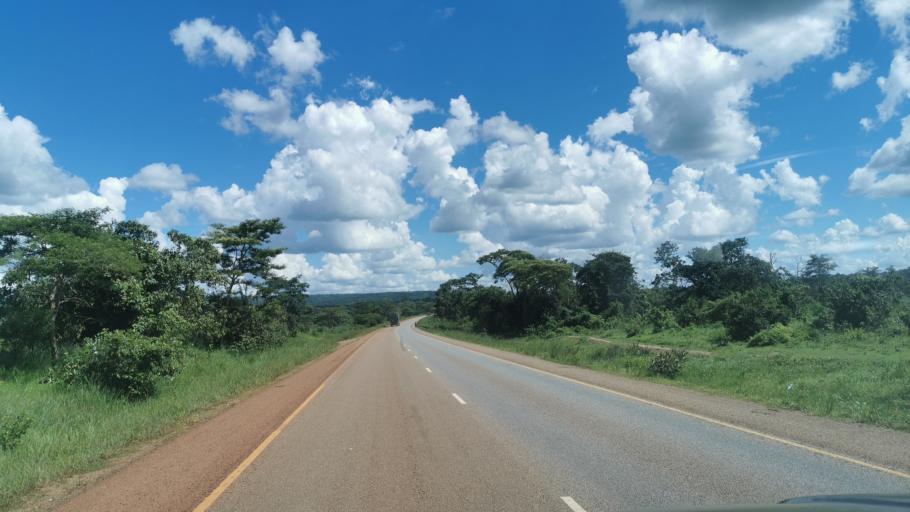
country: TZ
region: Geita
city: Uyovu
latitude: -3.0452
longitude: 31.2472
